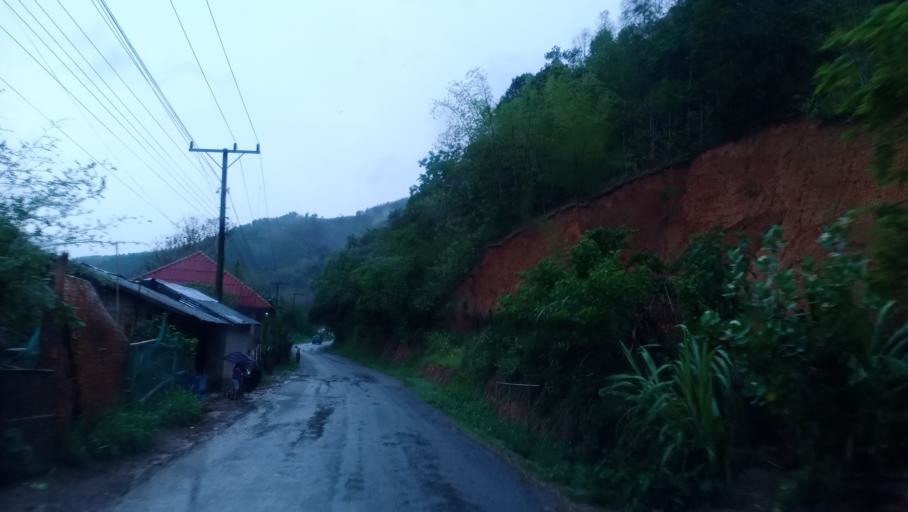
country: LA
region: Phongsali
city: Khoa
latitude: 21.0724
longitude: 102.4984
